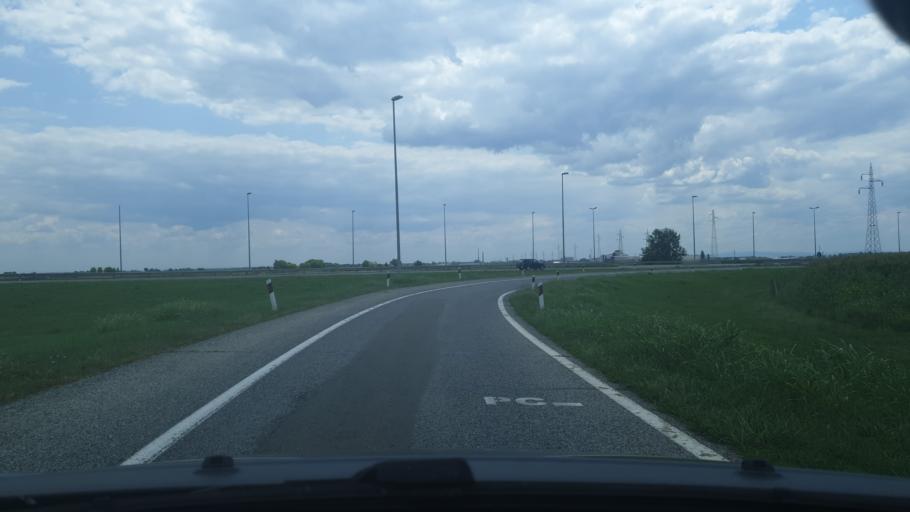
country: RS
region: Autonomna Pokrajina Vojvodina
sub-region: Sremski Okrug
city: Sremska Mitrovica
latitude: 44.9970
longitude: 19.6498
